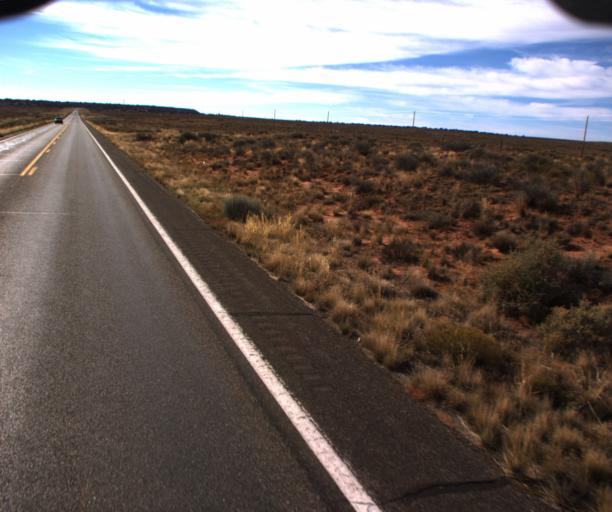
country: US
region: Arizona
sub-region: Coconino County
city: Kaibito
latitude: 36.6969
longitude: -111.2632
